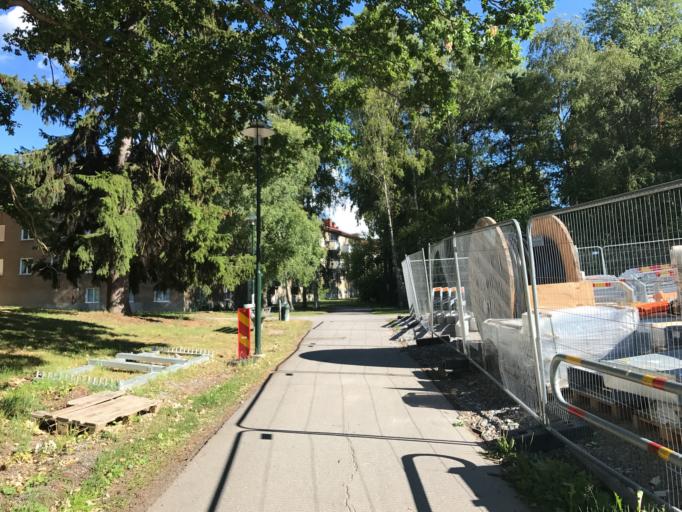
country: SE
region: Stockholm
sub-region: Huddinge Kommun
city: Segeltorp
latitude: 59.2971
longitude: 17.9704
